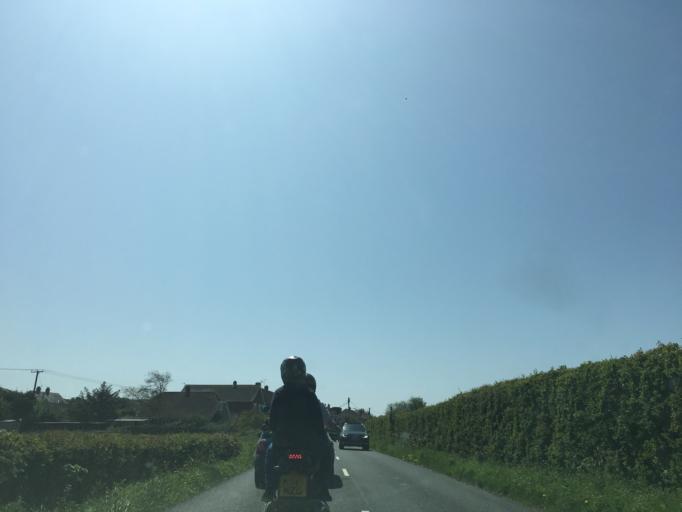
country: GB
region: England
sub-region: Isle of Wight
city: Niton
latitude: 50.5904
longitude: -1.2781
